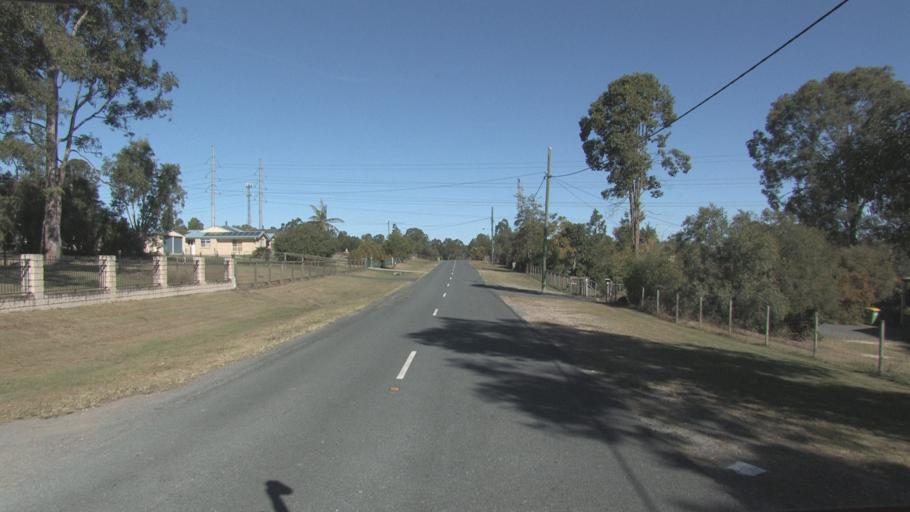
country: AU
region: Queensland
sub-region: Logan
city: North Maclean
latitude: -27.7313
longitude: 152.9612
